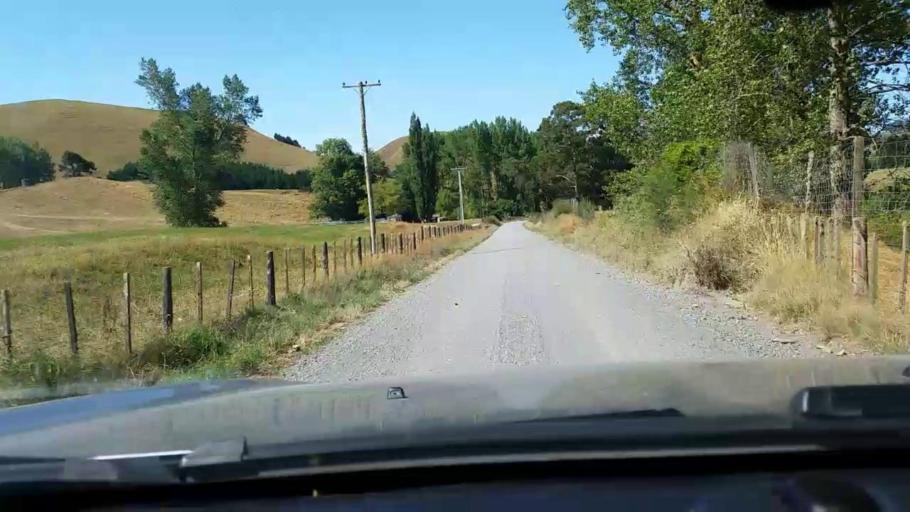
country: NZ
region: Bay of Plenty
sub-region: Rotorua District
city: Rotorua
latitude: -38.3715
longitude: 176.2068
